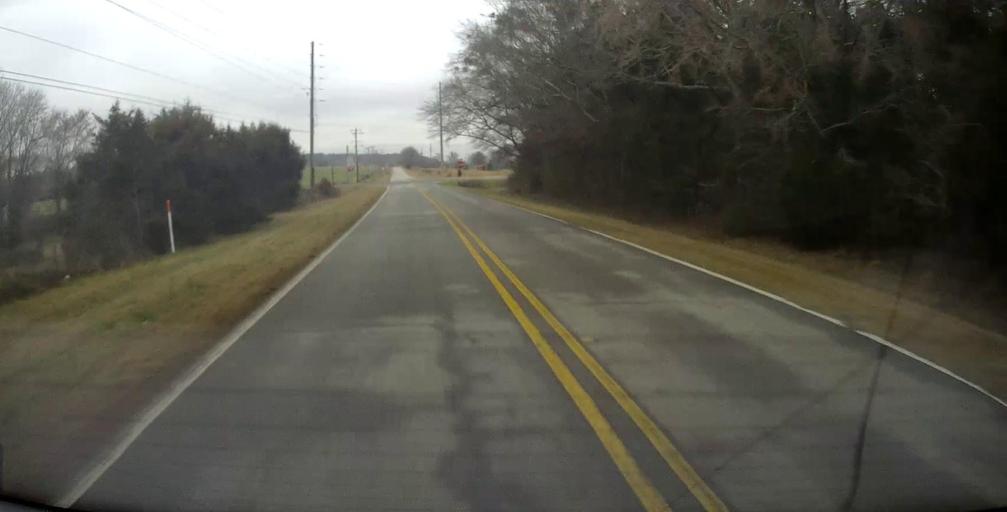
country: US
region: Georgia
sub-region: Lamar County
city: Barnesville
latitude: 33.0518
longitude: -84.1095
